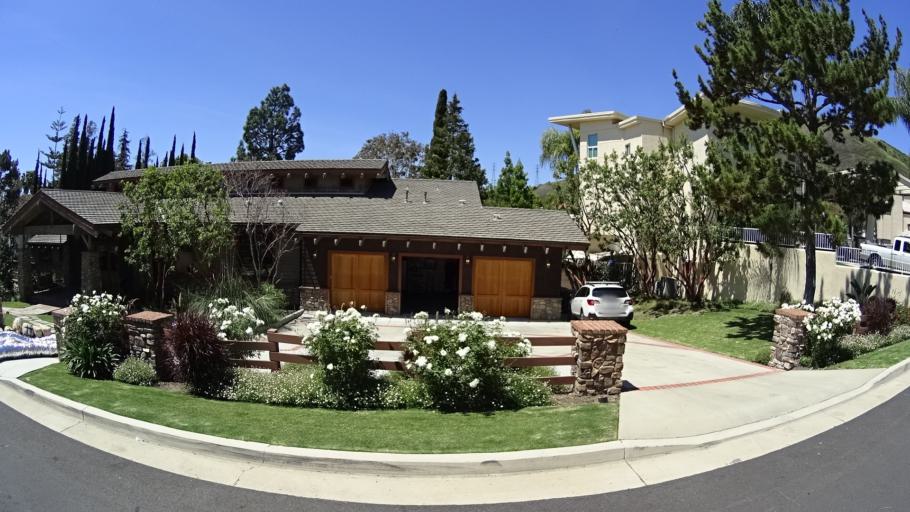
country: US
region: California
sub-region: Orange County
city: Villa Park
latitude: 33.8305
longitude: -117.8008
